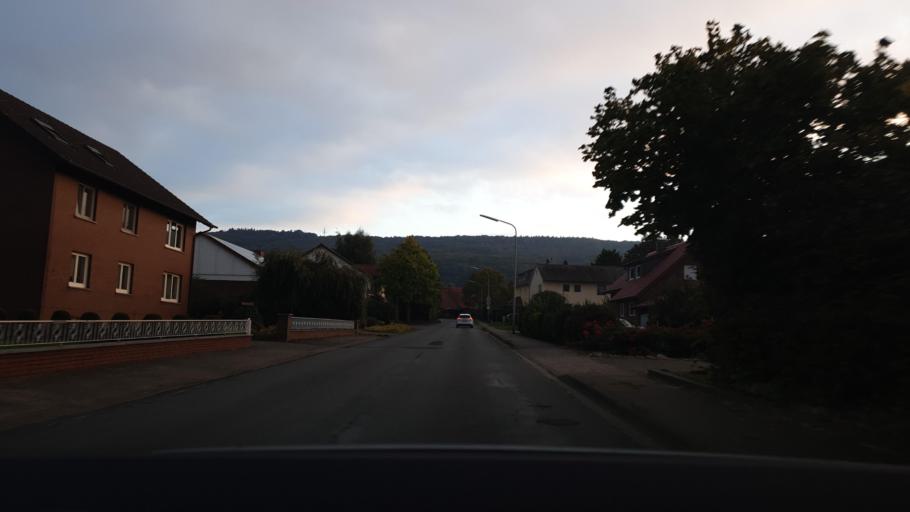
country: DE
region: North Rhine-Westphalia
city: Bad Oeynhausen
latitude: 52.2702
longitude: 8.8262
